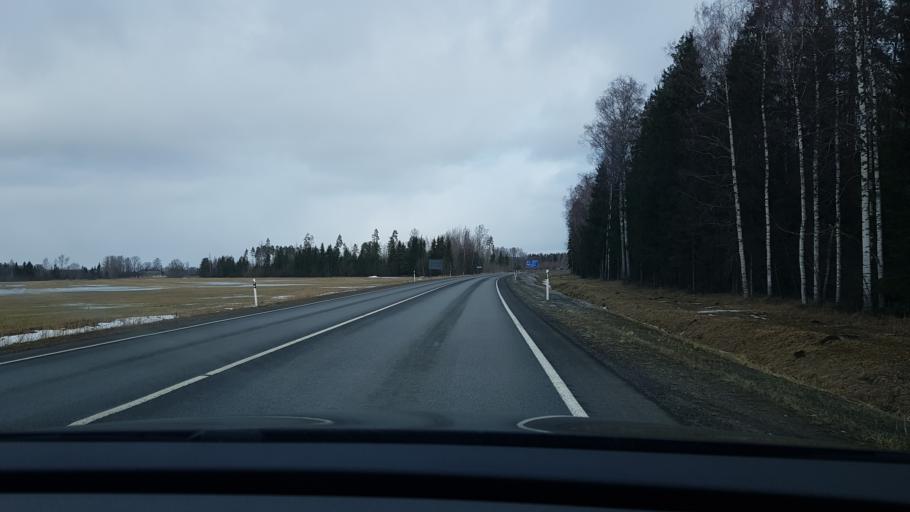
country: EE
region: Paernumaa
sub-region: Vaendra vald (alev)
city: Vandra
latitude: 58.6219
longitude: 24.9292
